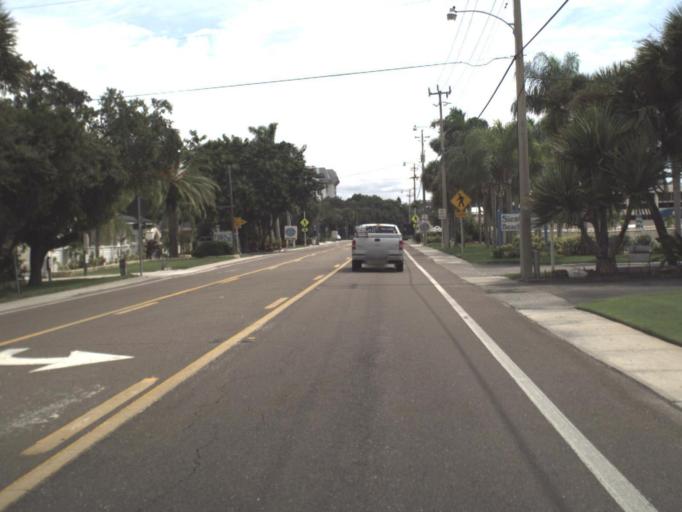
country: US
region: Florida
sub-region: Sarasota County
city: South Sarasota
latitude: 27.2634
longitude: -82.5418
